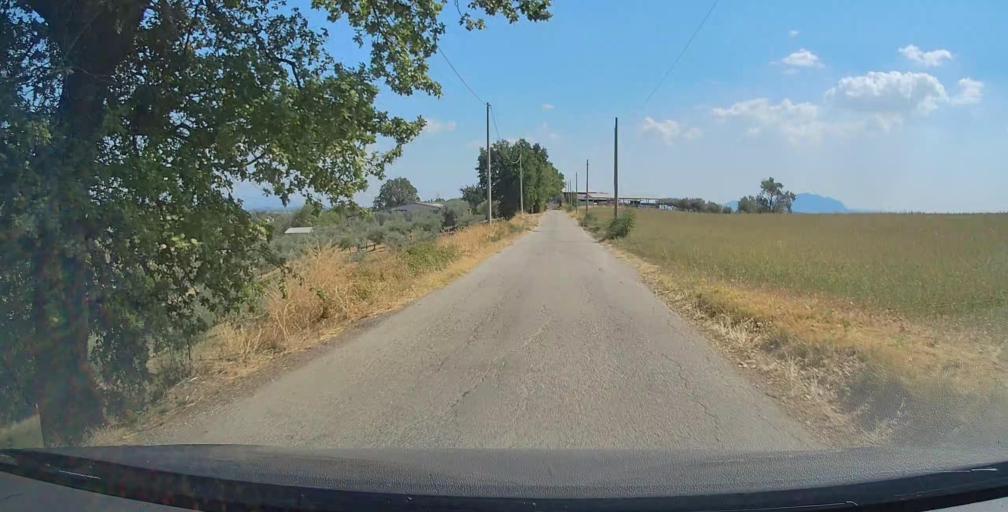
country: IT
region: Umbria
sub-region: Provincia di Terni
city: Calvi dell'Umbria
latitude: 42.3894
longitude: 12.5674
